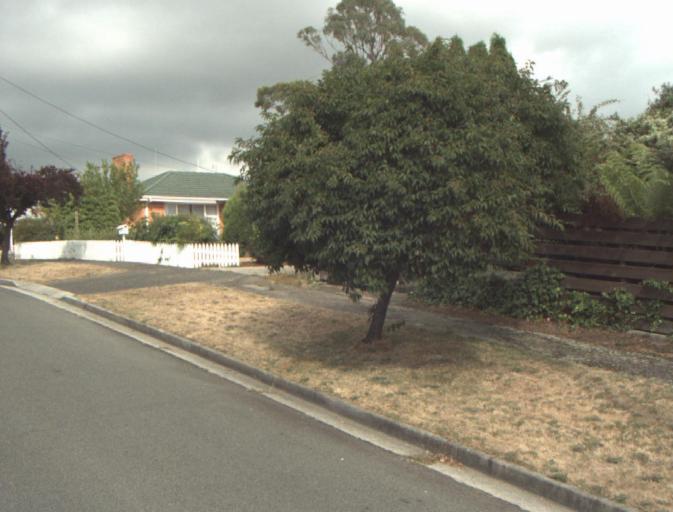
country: AU
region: Tasmania
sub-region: Launceston
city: East Launceston
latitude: -41.4781
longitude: 147.1718
